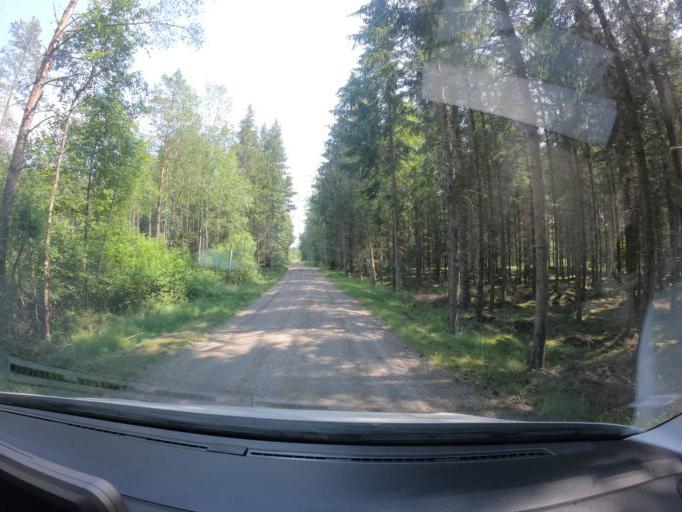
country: SE
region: Kronoberg
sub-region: Markaryds Kommun
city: Markaryd
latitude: 56.3882
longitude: 13.5413
